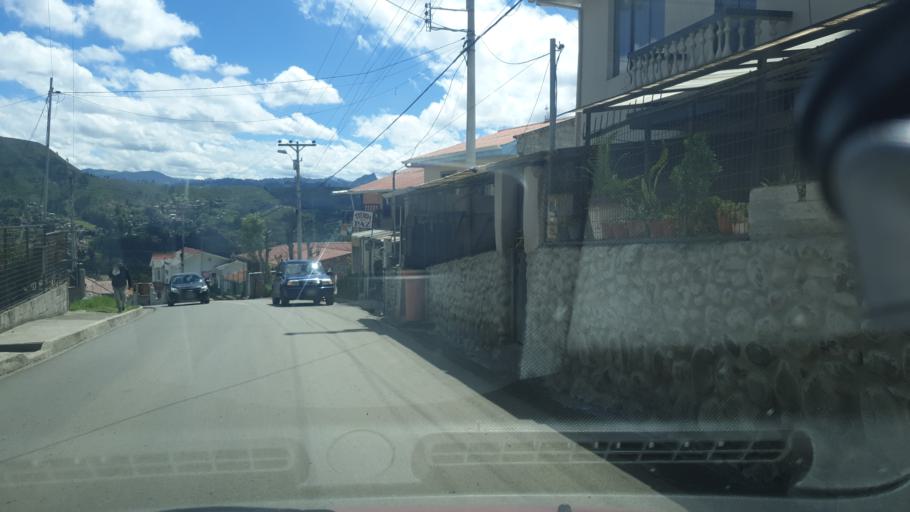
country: EC
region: Azuay
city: Llacao
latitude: -2.8628
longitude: -78.9070
